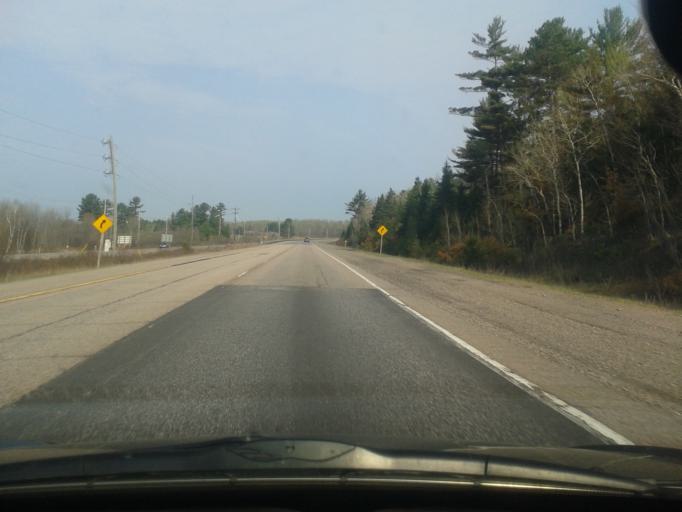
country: CA
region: Ontario
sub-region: Nipissing District
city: North Bay
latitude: 46.2867
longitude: -79.4140
